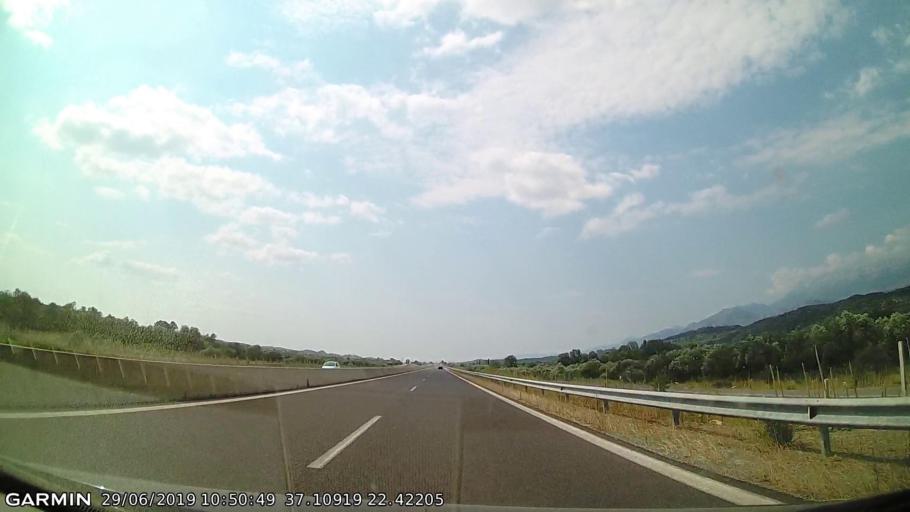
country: GR
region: Peloponnese
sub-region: Nomos Lakonias
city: Magoula
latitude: 37.1089
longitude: 22.4222
